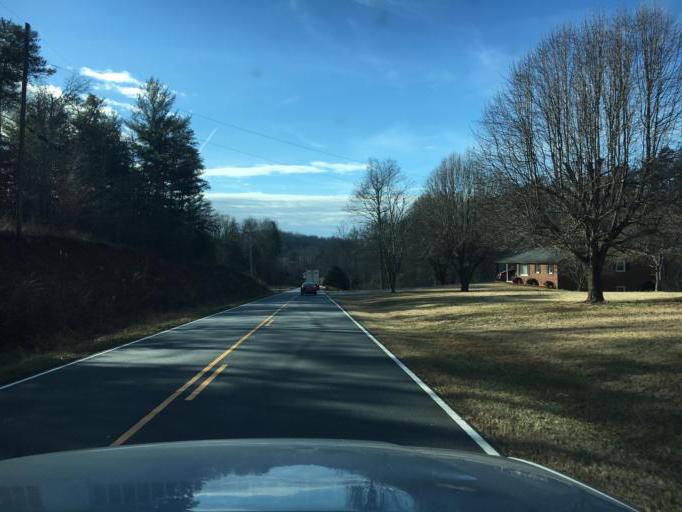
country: US
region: North Carolina
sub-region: Rutherford County
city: Spindale
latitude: 35.4960
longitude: -81.8656
